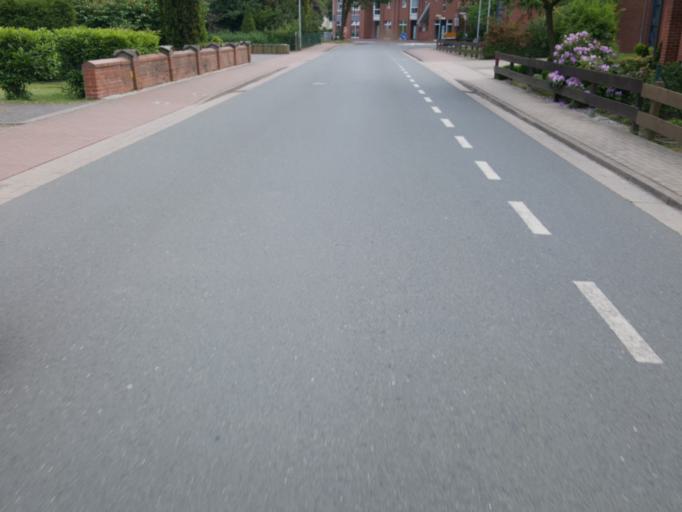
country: DE
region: Lower Saxony
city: Stolzenau
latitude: 52.5128
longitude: 9.0689
